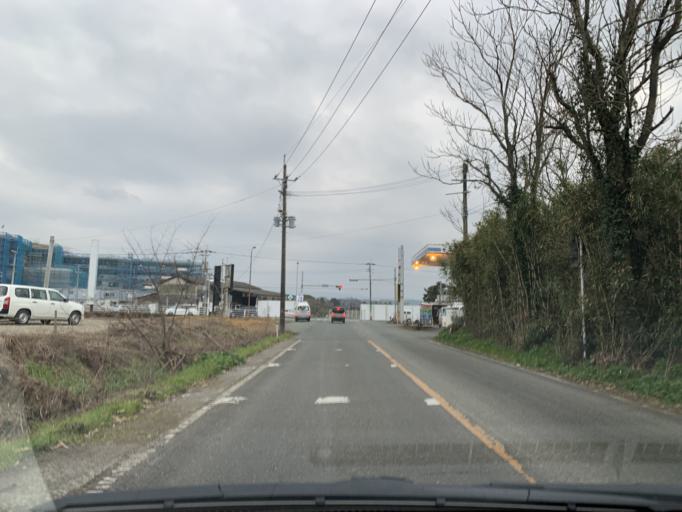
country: JP
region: Kumamoto
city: Ozu
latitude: 32.8744
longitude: 130.8474
